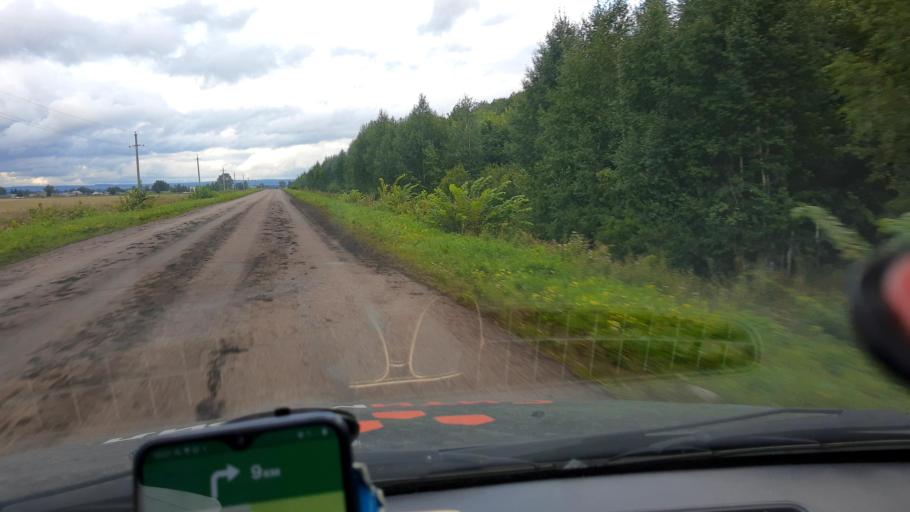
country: RU
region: Bashkortostan
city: Tolbazy
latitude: 53.9870
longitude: 56.2588
